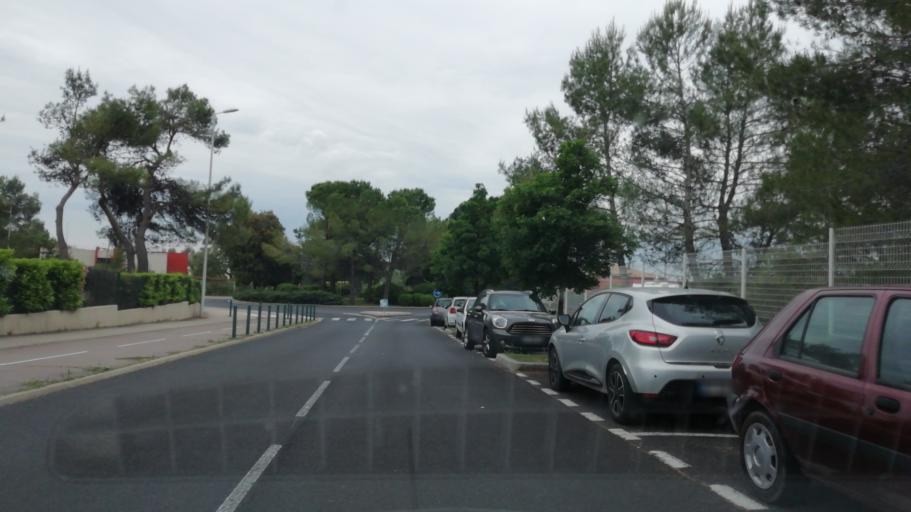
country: FR
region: Languedoc-Roussillon
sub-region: Departement de l'Herault
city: Saint-Clement-de-Riviere
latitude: 43.7096
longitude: 3.8322
